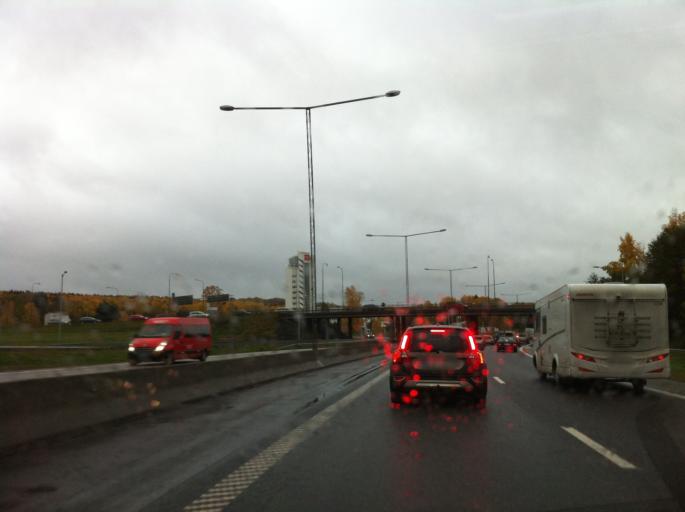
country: SE
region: Joenkoeping
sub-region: Jonkopings Kommun
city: Jonkoping
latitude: 57.7702
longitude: 14.1901
